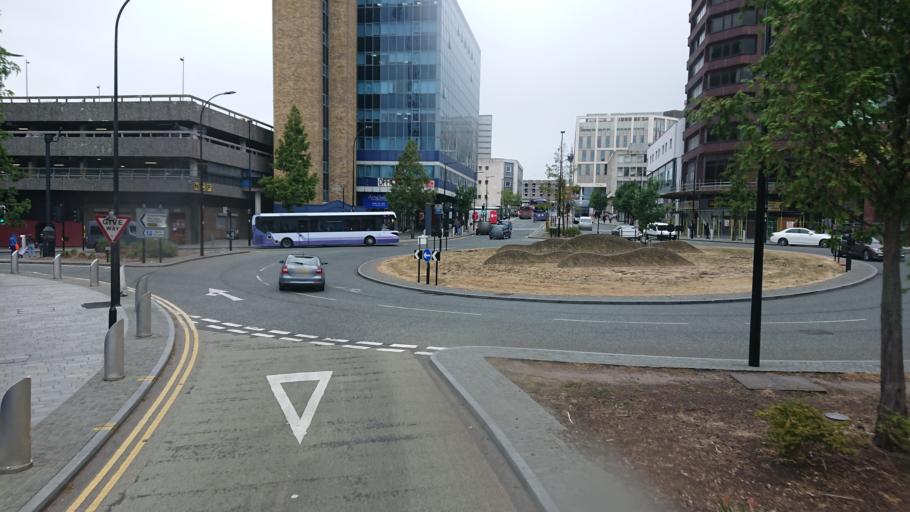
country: GB
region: England
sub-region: Sheffield
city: Sheffield
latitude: 53.3772
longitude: -1.4697
